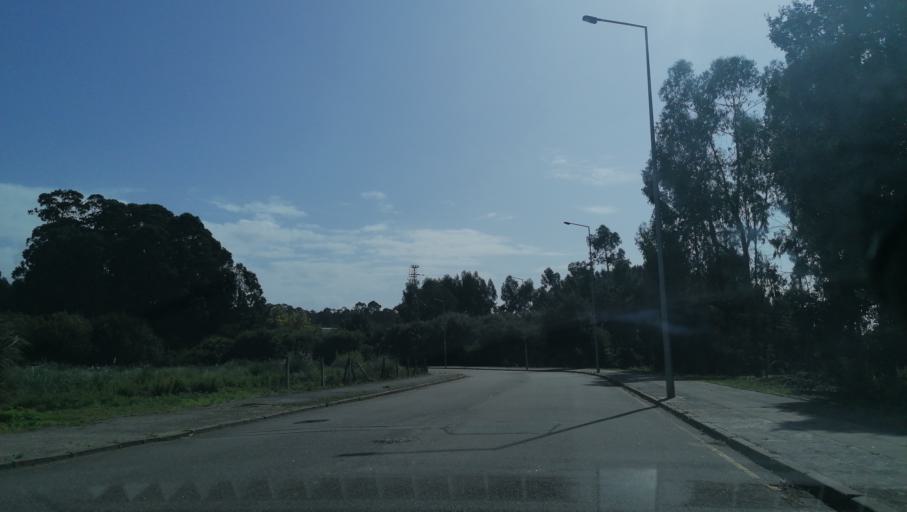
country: PT
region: Aveiro
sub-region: Espinho
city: Silvalde
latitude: 41.0022
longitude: -8.6235
